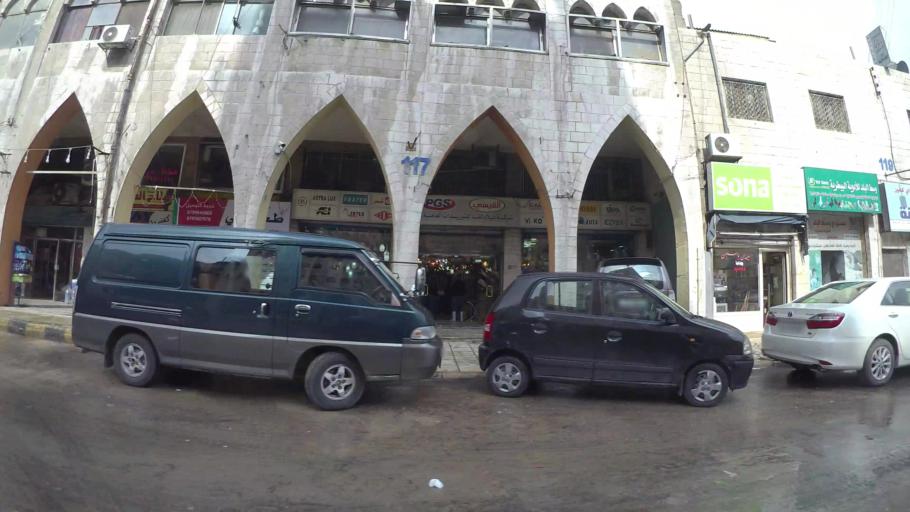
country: JO
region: Amman
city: Amman
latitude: 31.9511
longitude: 35.9370
